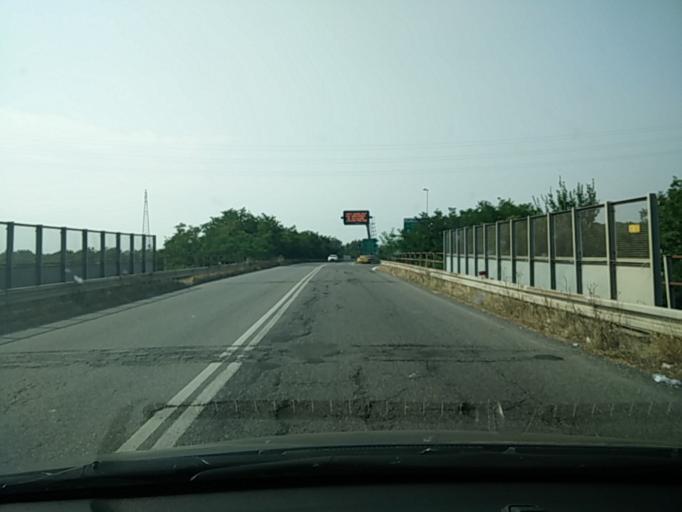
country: IT
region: Lombardy
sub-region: Provincia di Pavia
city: Broni
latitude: 45.0758
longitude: 9.2745
